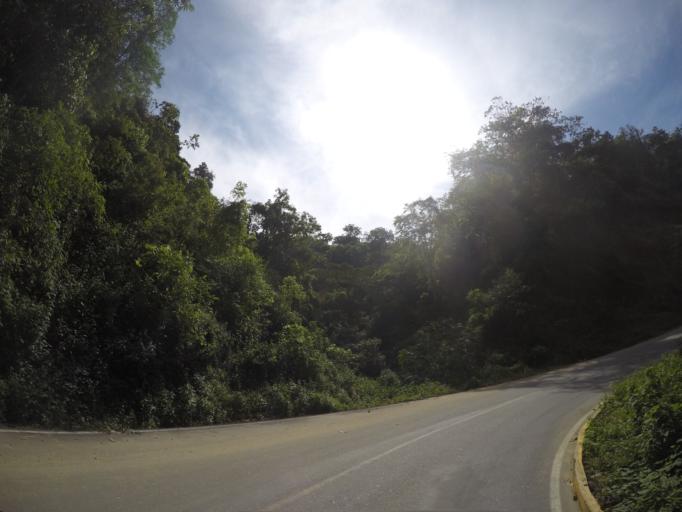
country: MX
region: Oaxaca
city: Pluma Hidalgo
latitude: 15.9320
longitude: -96.4211
